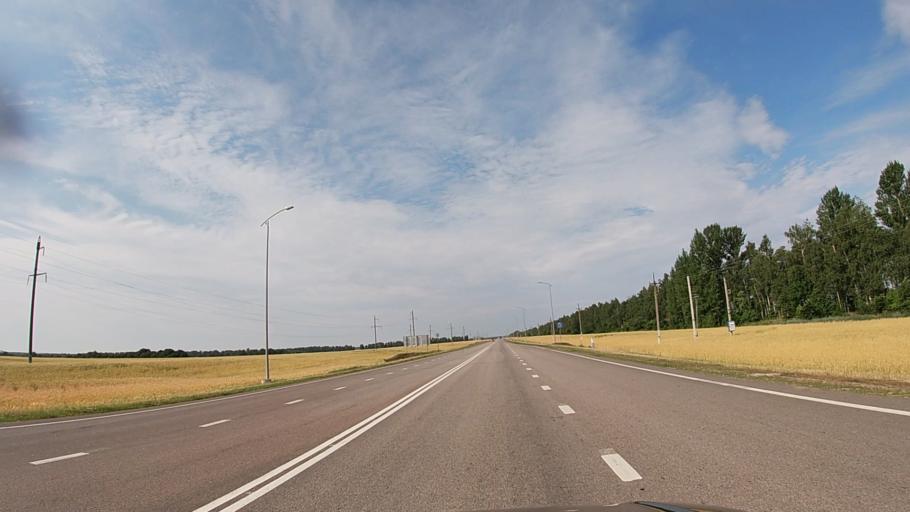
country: RU
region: Belgorod
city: Proletarskiy
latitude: 50.8304
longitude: 35.7661
